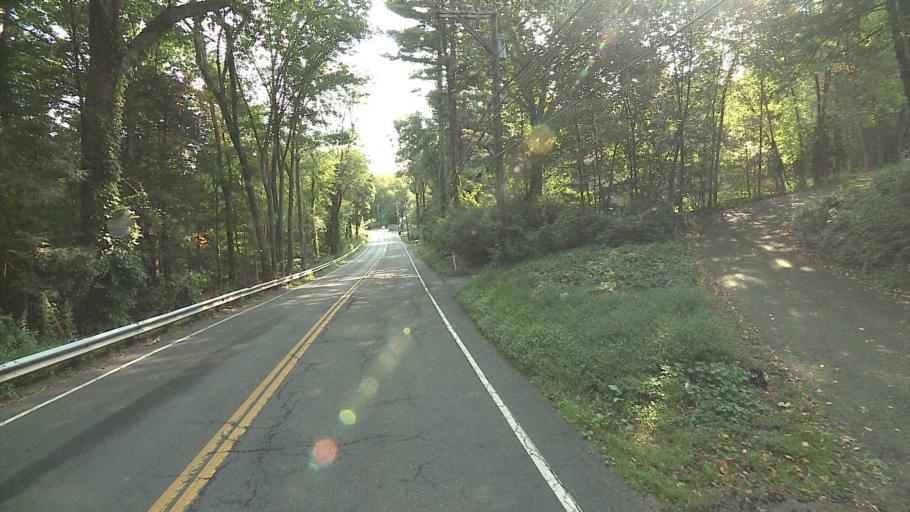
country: US
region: Connecticut
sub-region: Fairfield County
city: Newtown
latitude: 41.4350
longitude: -73.2732
